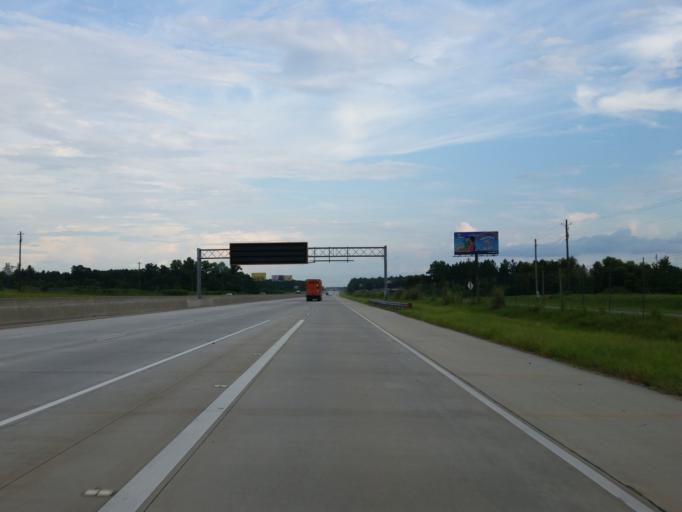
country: US
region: Georgia
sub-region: Cook County
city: Adel
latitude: 31.1092
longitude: -83.4262
